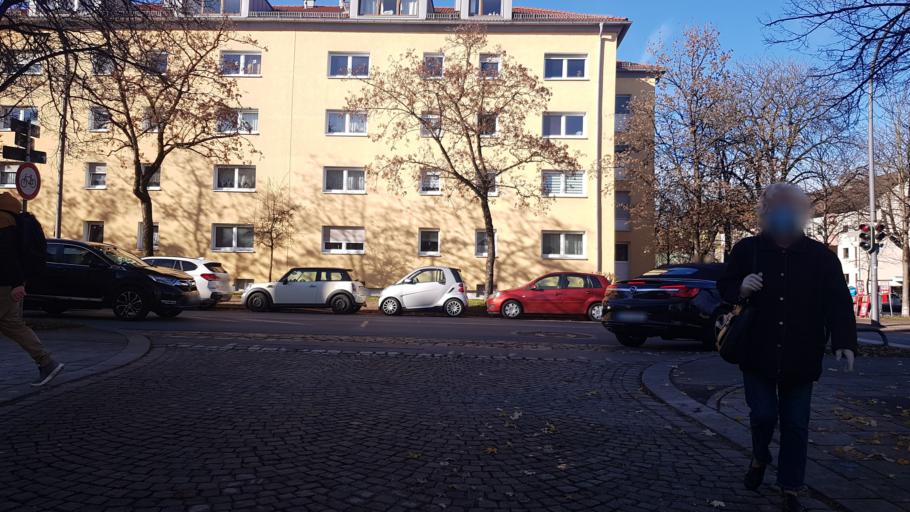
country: DE
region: Bavaria
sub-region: Upper Bavaria
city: Karlsfeld
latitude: 48.1777
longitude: 11.5104
